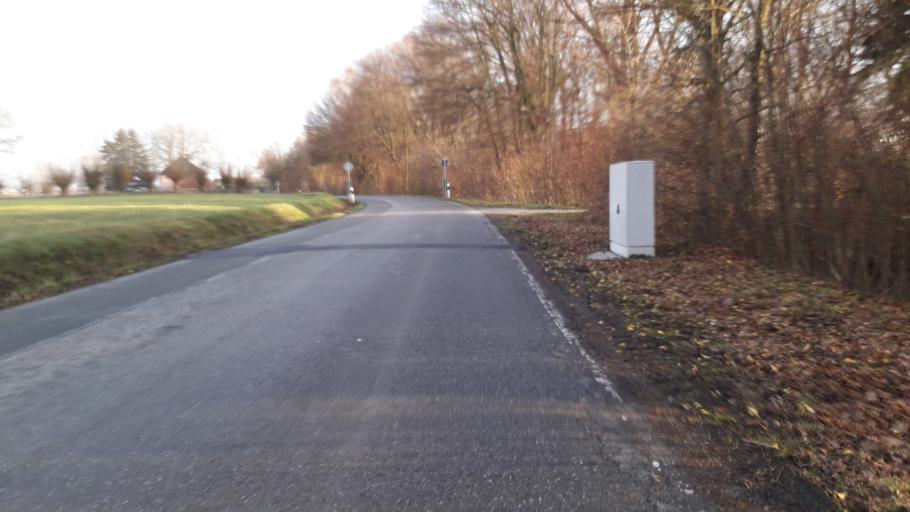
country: DE
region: North Rhine-Westphalia
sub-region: Regierungsbezirk Arnsberg
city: Soest
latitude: 51.5698
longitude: 8.0464
